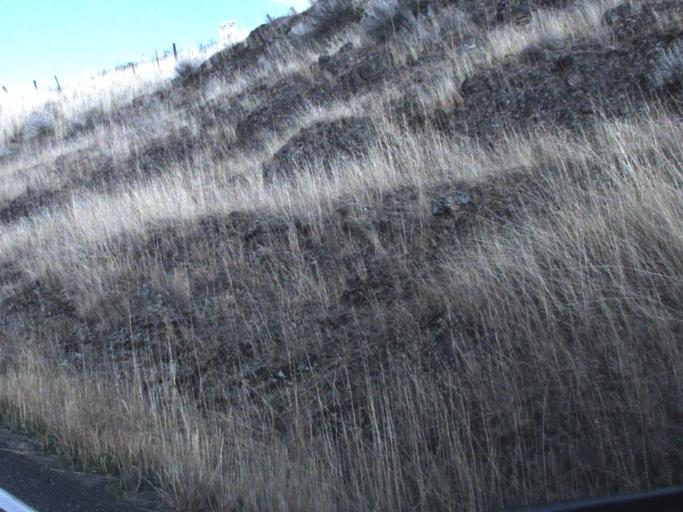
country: US
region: Washington
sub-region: Stevens County
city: Kettle Falls
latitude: 48.4095
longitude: -118.1716
